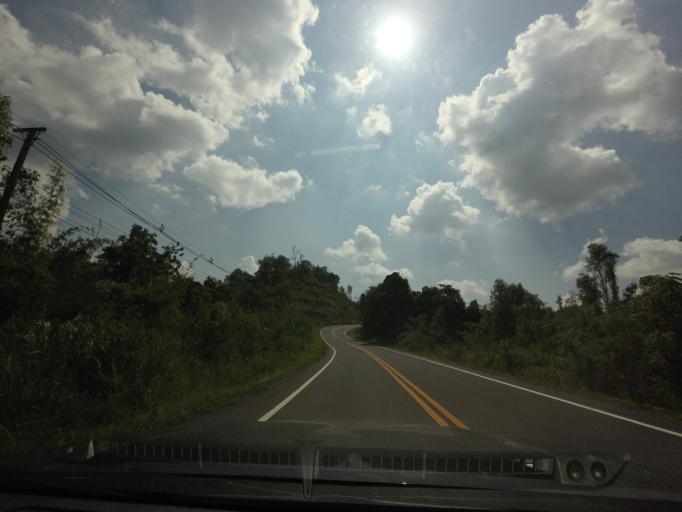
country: TH
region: Nan
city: Bo Kluea
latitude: 19.0793
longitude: 101.1433
